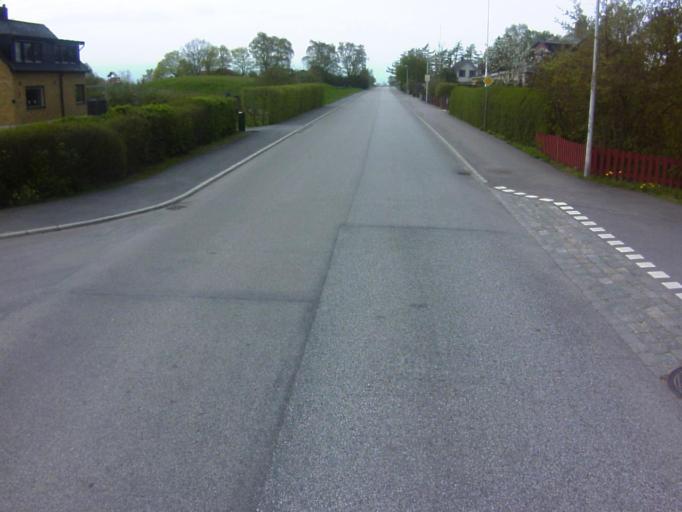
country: SE
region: Skane
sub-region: Kavlinge Kommun
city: Loddekopinge
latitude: 55.7577
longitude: 13.0138
